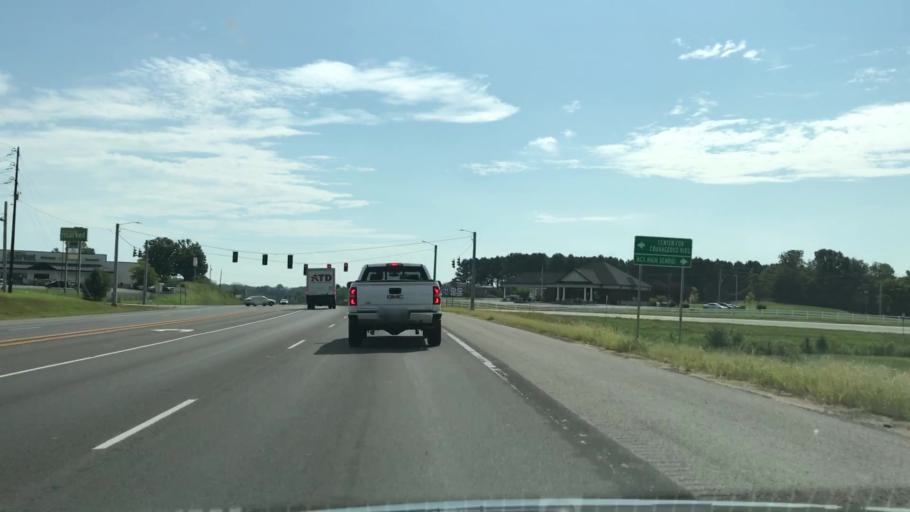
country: US
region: Kentucky
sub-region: Allen County
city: Scottsville
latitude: 36.7563
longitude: -86.2187
